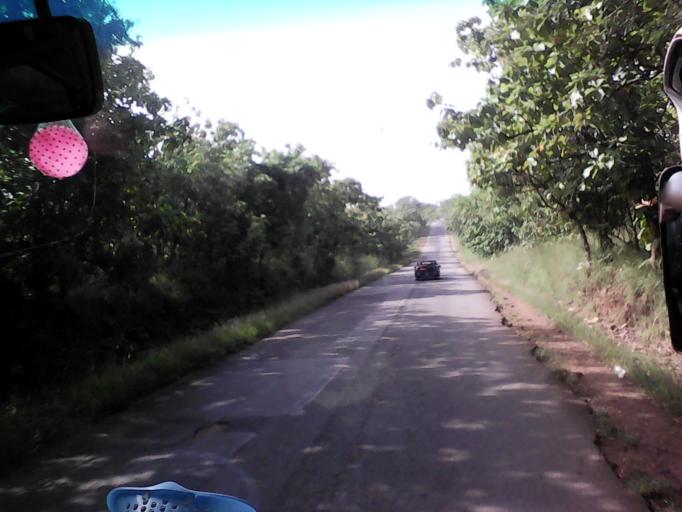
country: TG
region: Centrale
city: Sokode
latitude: 9.1243
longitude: 1.1471
